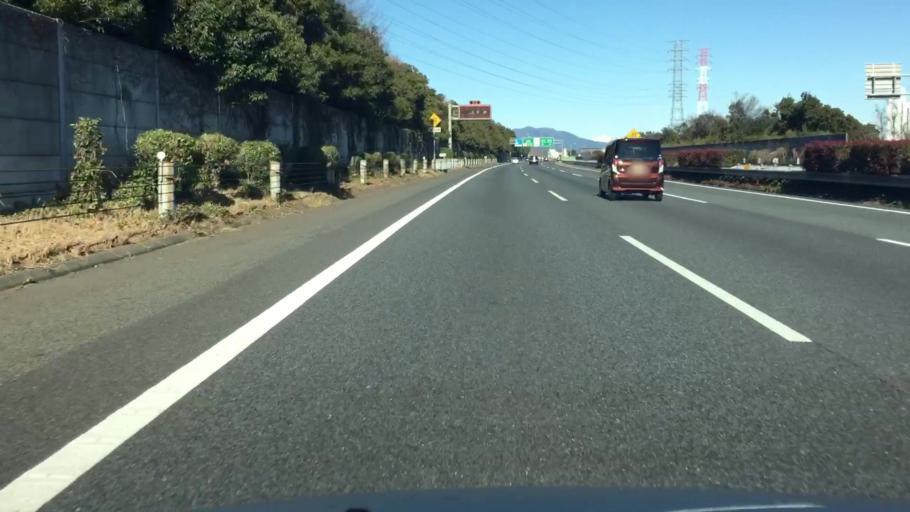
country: JP
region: Gunma
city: Takasaki
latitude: 36.3683
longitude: 139.0301
